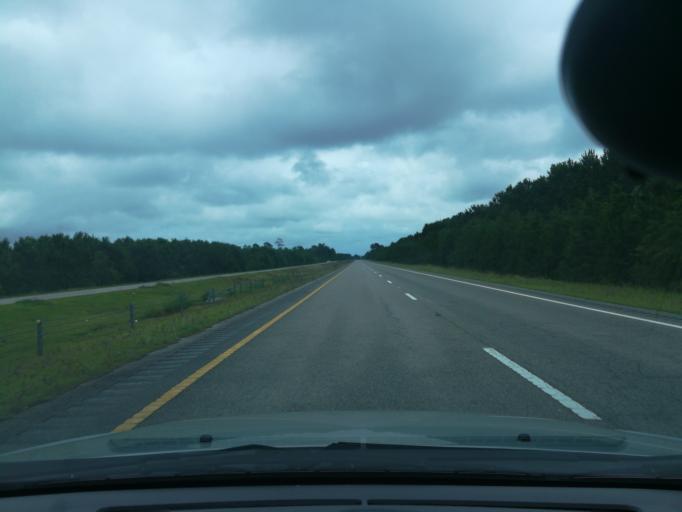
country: US
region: North Carolina
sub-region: Chowan County
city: Edenton
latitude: 35.8964
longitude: -76.5101
